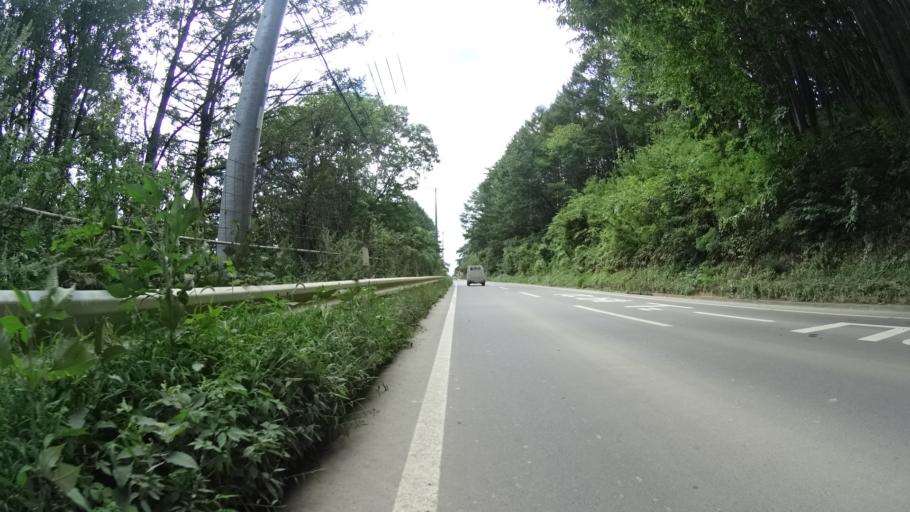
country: JP
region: Nagano
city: Saku
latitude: 35.9640
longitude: 138.5356
